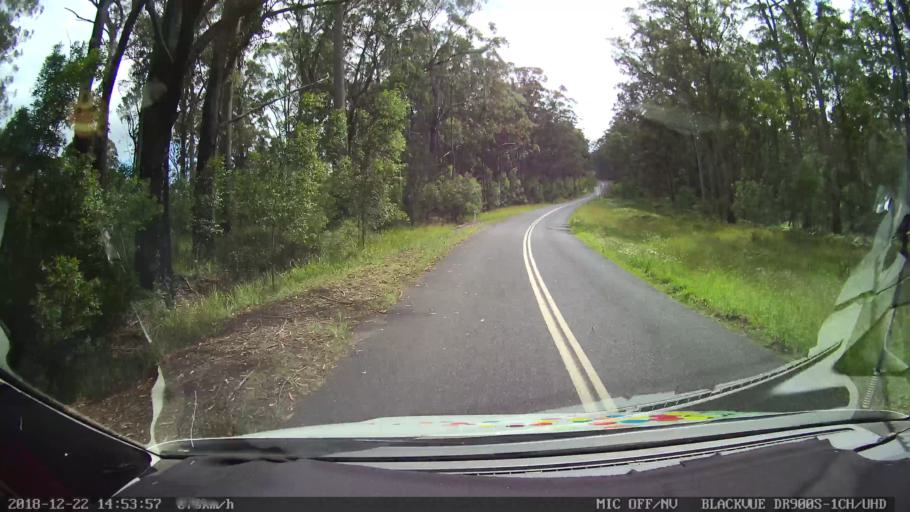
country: AU
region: New South Wales
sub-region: Bellingen
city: Dorrigo
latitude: -30.2227
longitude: 152.5374
